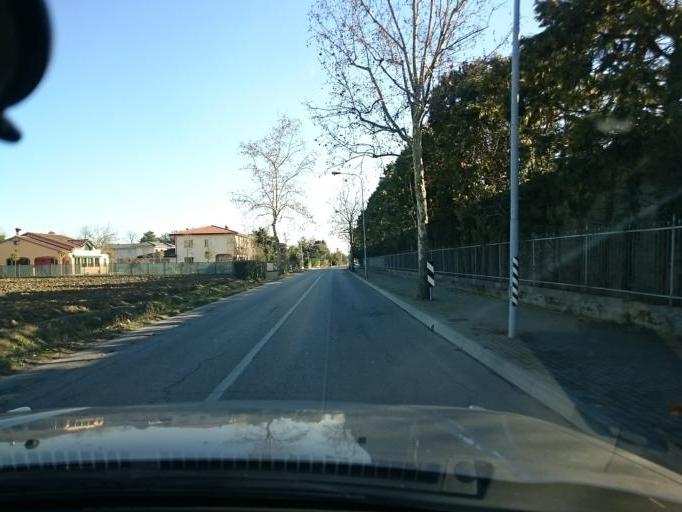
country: IT
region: Veneto
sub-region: Provincia di Padova
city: Montegrotto Terme
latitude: 45.3365
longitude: 11.7927
